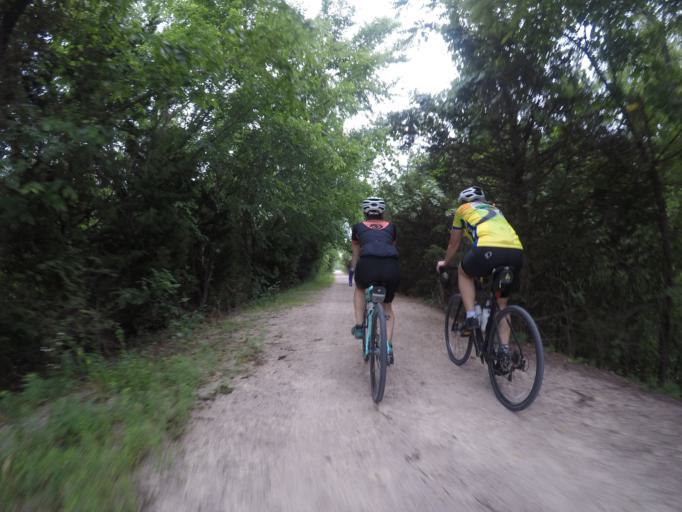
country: US
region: Kansas
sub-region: Anderson County
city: Garnett
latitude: 38.2928
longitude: -95.2426
